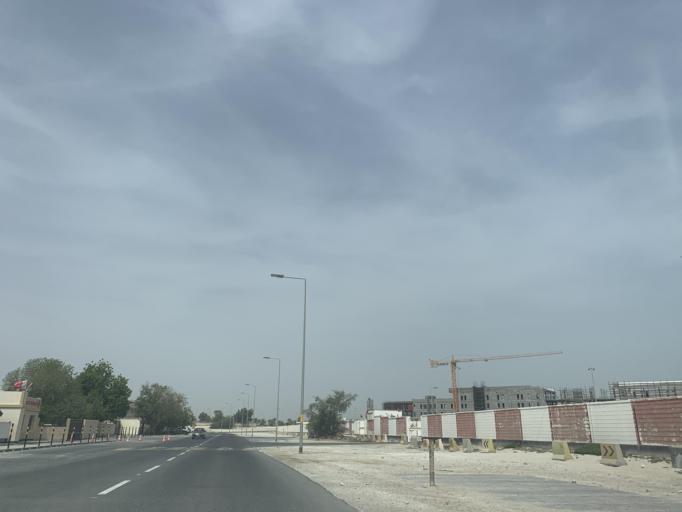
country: BH
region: Northern
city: Madinat `Isa
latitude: 26.1596
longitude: 50.5429
